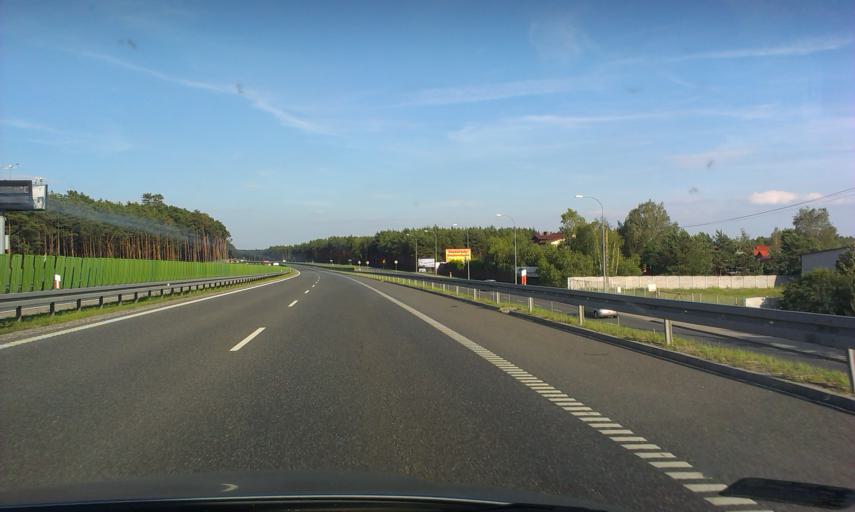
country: PL
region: Kujawsko-Pomorskie
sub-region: Powiat bydgoski
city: Biale Blota
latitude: 53.0580
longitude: 17.9635
